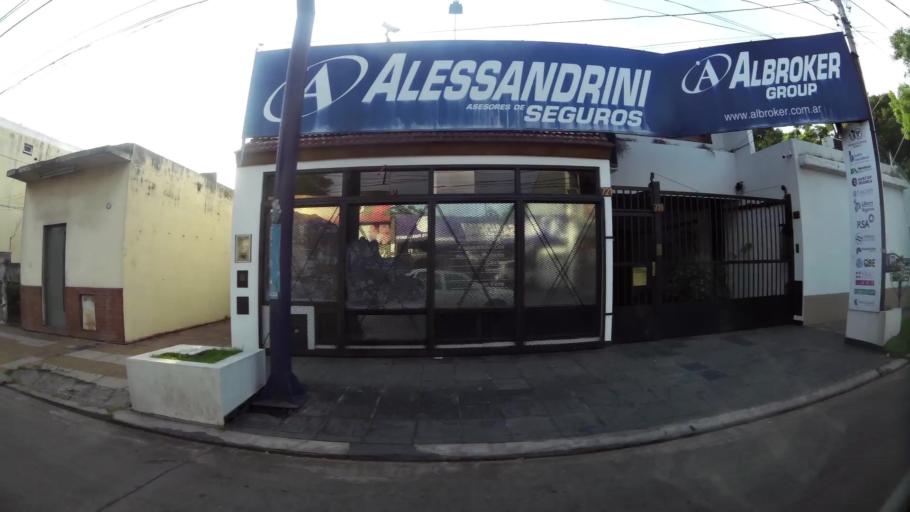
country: AR
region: Buenos Aires
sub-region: Partido de Moron
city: Moron
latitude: -34.6559
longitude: -58.6300
